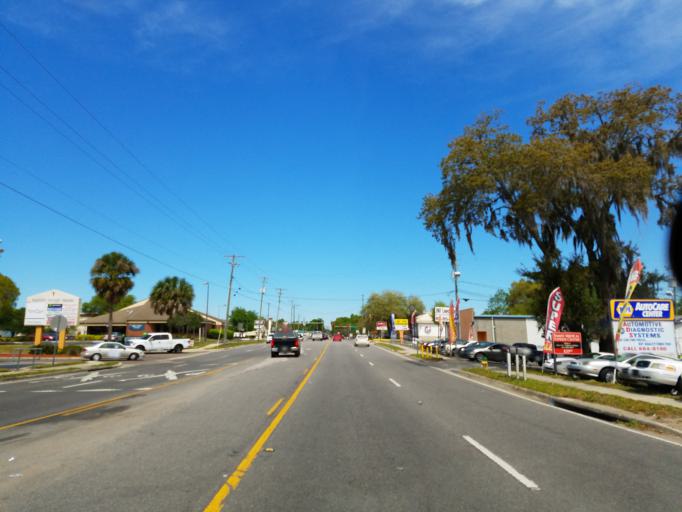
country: US
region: Florida
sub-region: Hillsborough County
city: Seffner
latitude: 27.9796
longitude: -82.2859
